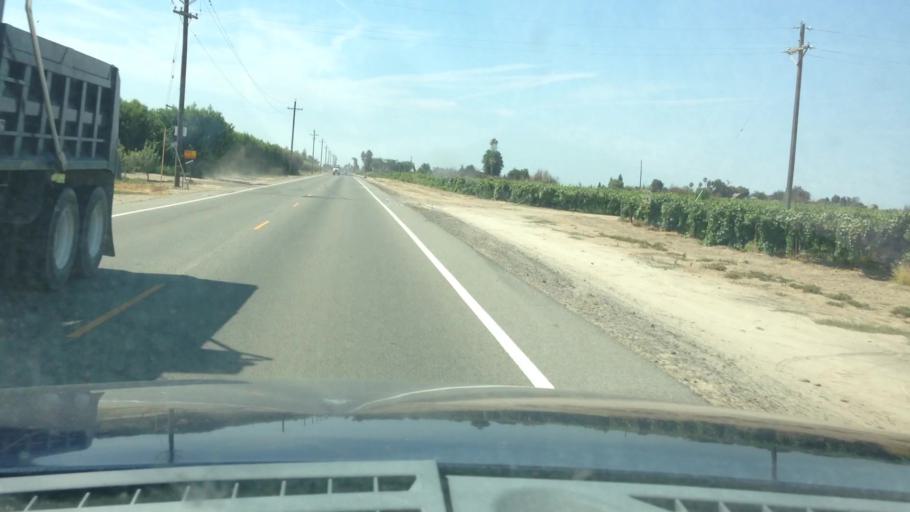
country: US
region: California
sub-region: Fresno County
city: Parlier
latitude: 36.5767
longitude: -119.5572
